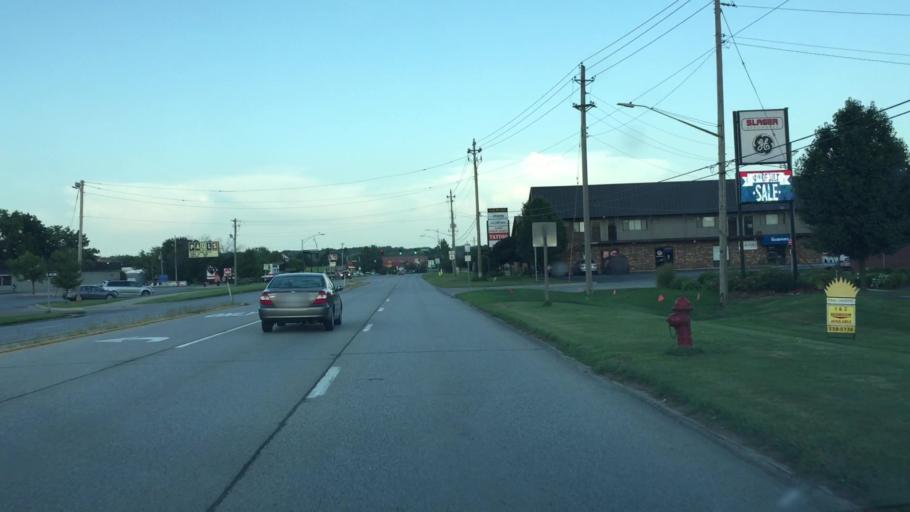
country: US
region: Iowa
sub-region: Johnson County
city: University Heights
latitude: 41.6474
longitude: -91.5447
